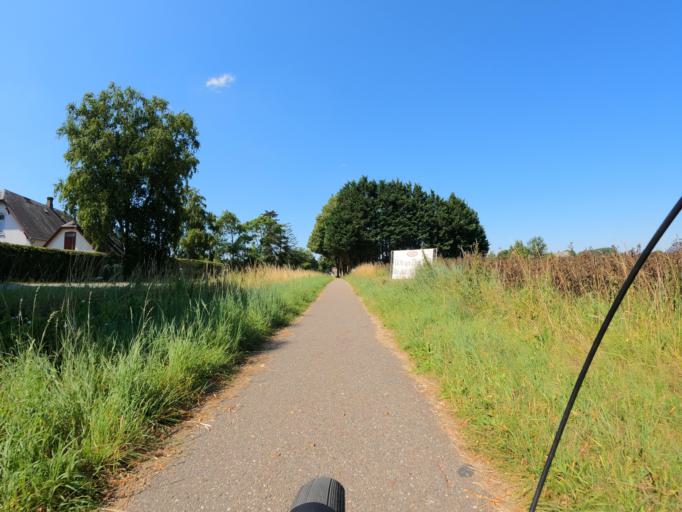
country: DE
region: Schleswig-Holstein
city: Steinbergkirche
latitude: 54.7542
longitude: 9.7685
